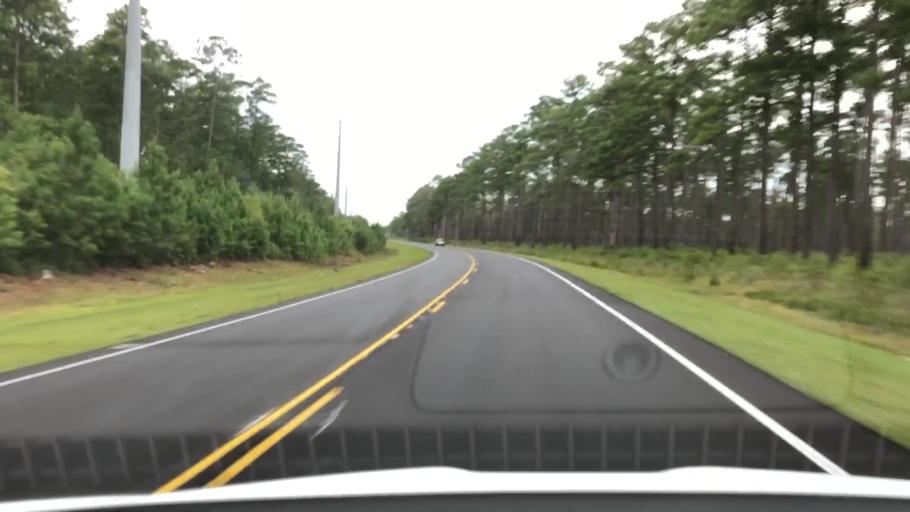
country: US
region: North Carolina
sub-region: Onslow County
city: Swansboro
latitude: 34.7752
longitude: -77.0999
